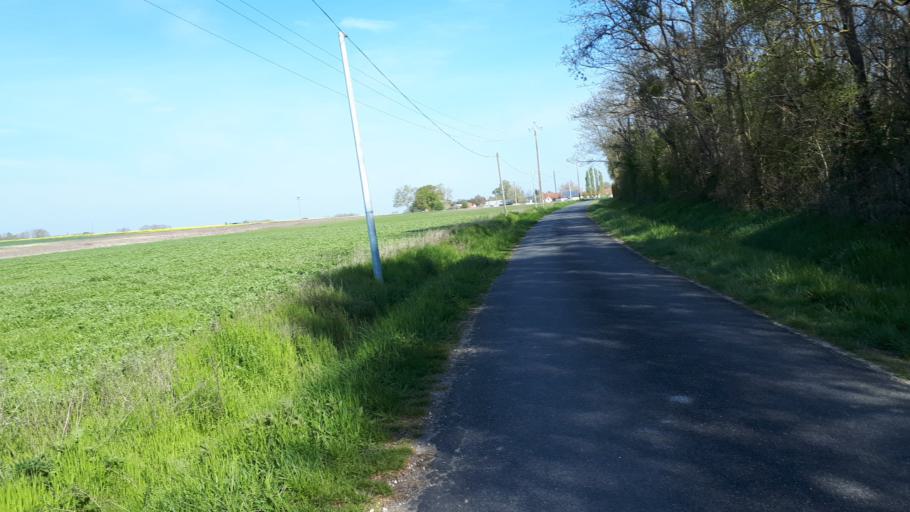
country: FR
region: Centre
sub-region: Departement du Loir-et-Cher
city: Contres
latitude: 47.3768
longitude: 1.3949
